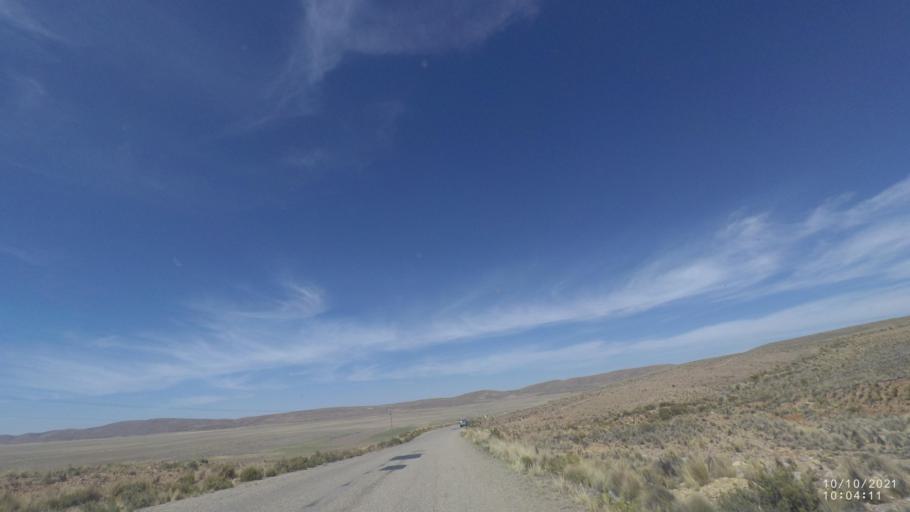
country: BO
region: La Paz
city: Eucaliptus
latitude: -17.3801
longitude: -67.4431
